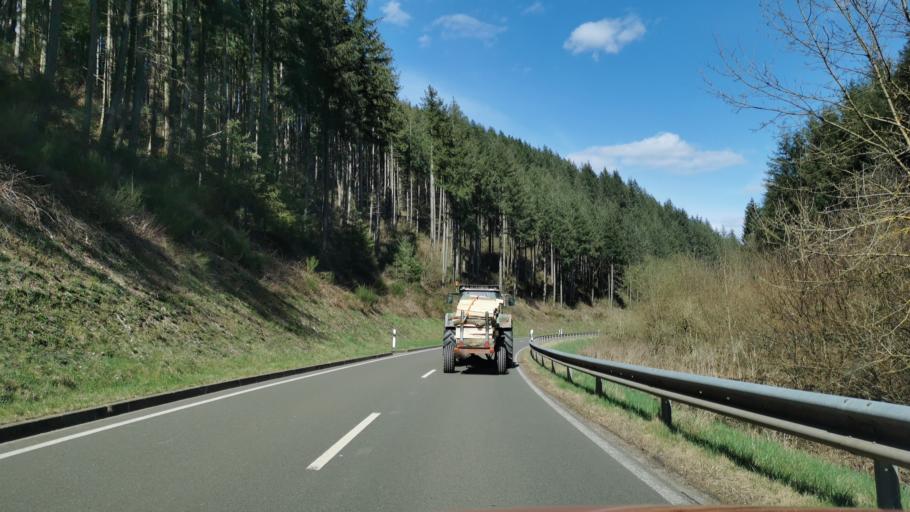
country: DE
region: Rheinland-Pfalz
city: Bruch
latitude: 49.9405
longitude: 6.7818
